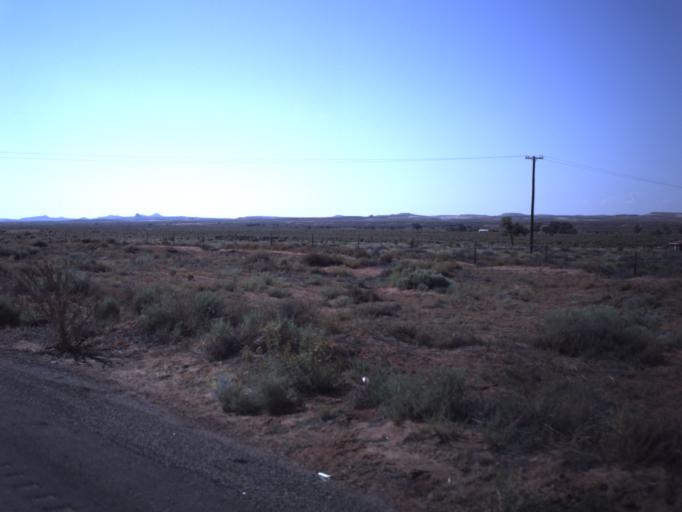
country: US
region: Utah
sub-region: San Juan County
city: Blanding
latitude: 37.1562
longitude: -109.5701
